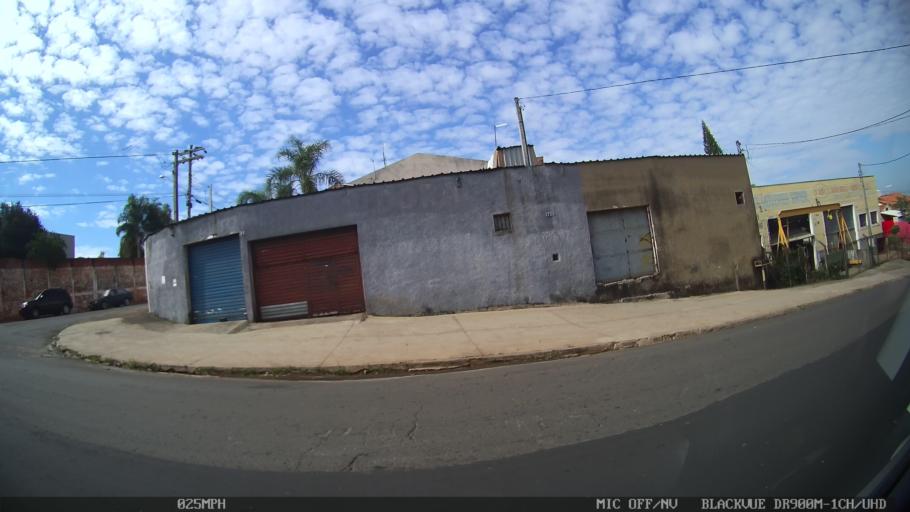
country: BR
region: Sao Paulo
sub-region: Santa Barbara D'Oeste
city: Santa Barbara d'Oeste
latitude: -22.7711
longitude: -47.4037
